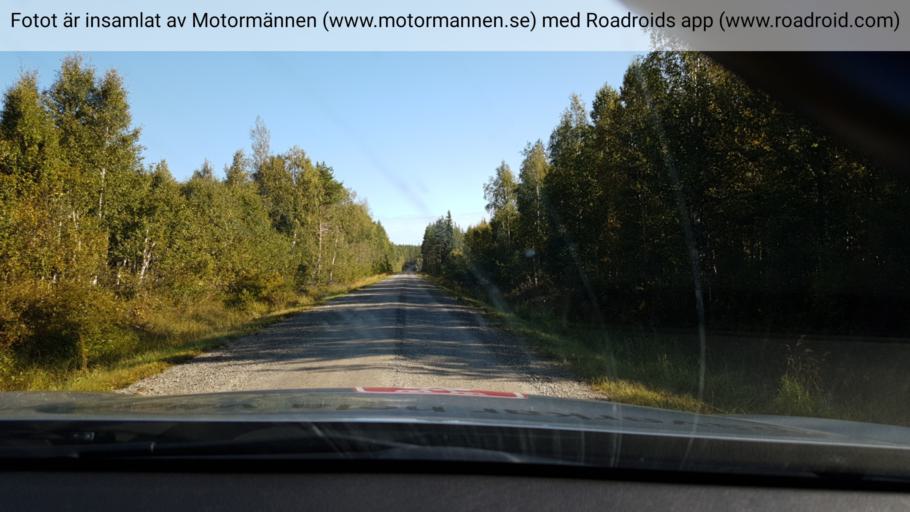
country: SE
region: Vaesterbotten
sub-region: Norsjo Kommun
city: Norsjoe
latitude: 64.6843
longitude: 19.4097
